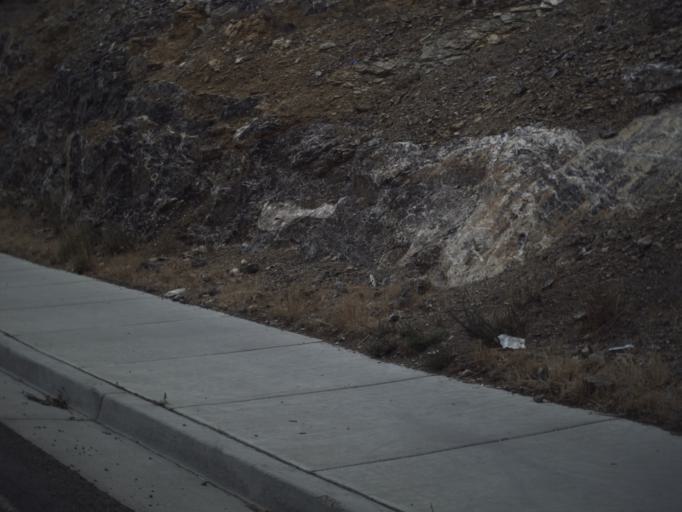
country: US
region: Utah
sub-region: Tooele County
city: Wendover
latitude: 40.7391
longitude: -114.0433
